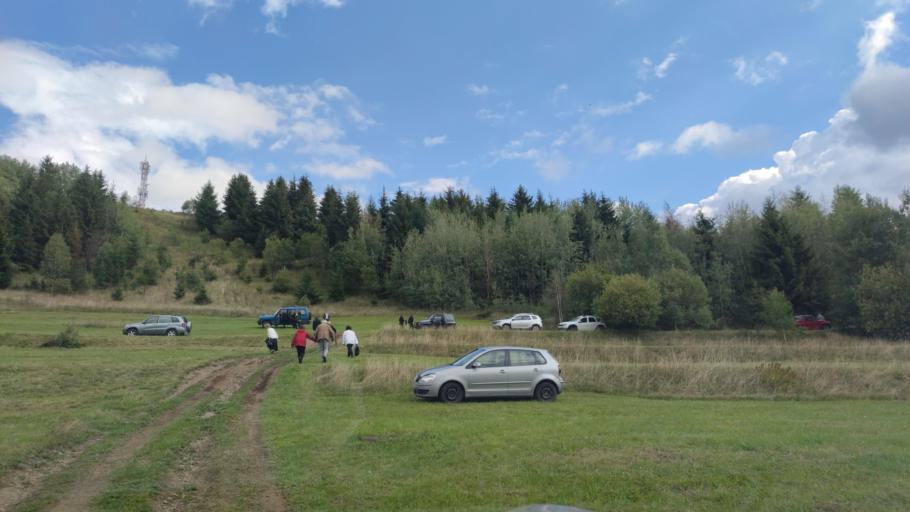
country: RO
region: Harghita
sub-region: Municipiul Gheorgheni
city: Gheorgheni
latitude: 46.7208
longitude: 25.6363
